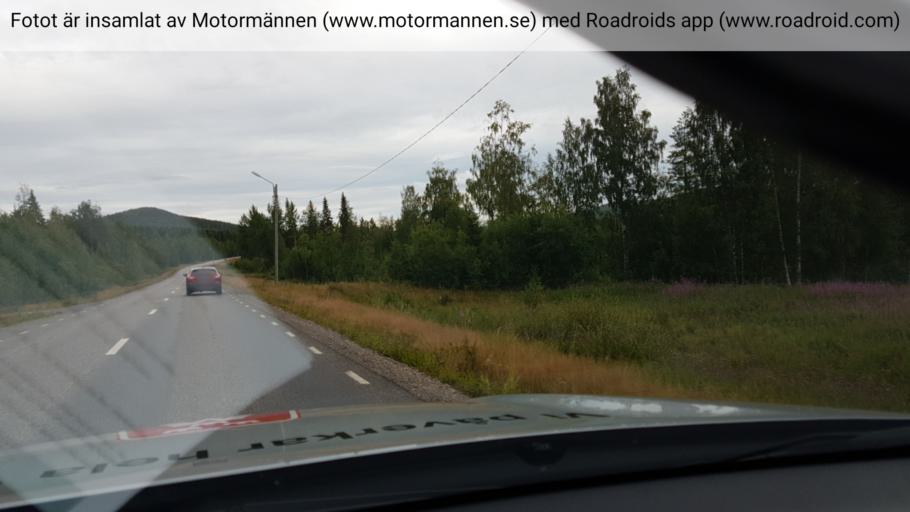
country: SE
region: Norrbotten
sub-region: Overkalix Kommun
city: OEverkalix
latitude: 66.5713
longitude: 22.7594
